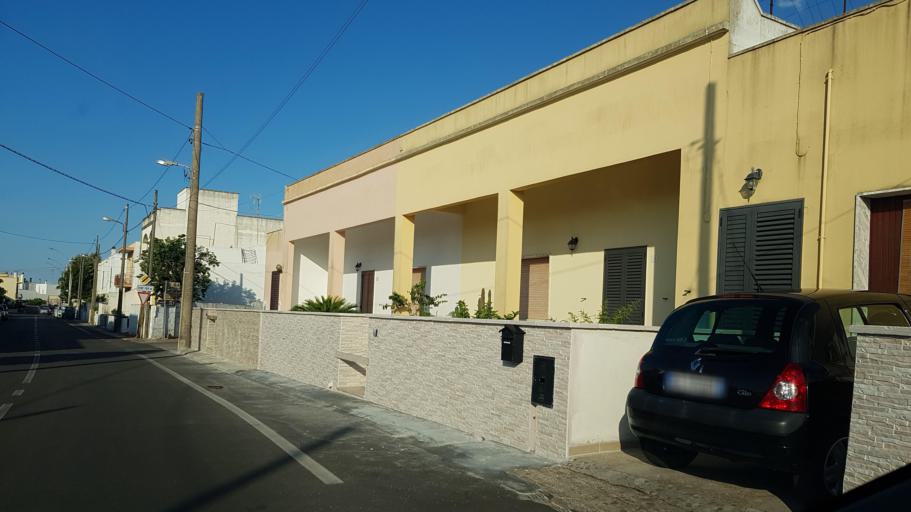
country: IT
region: Apulia
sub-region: Provincia di Lecce
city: Andrano
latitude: 39.9825
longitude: 18.3770
